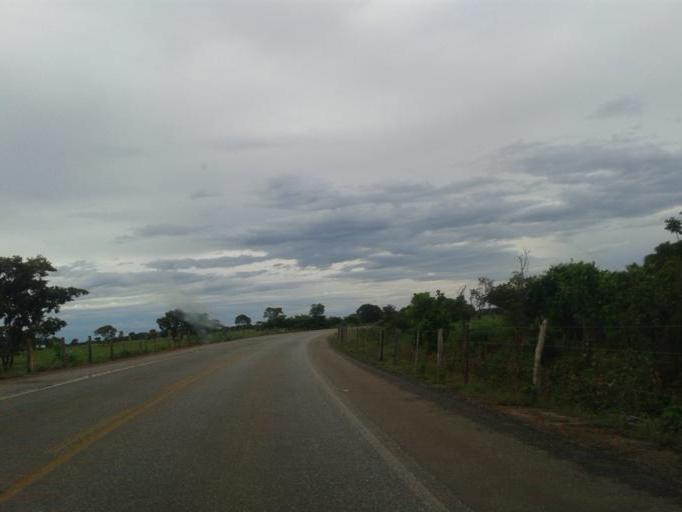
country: BR
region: Goias
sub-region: Mozarlandia
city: Mozarlandia
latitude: -14.7994
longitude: -50.5350
